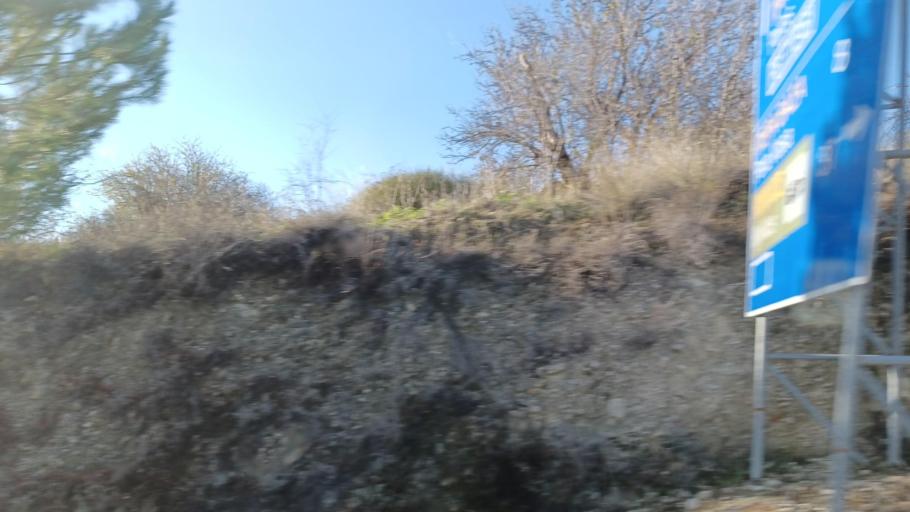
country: CY
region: Limassol
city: Pachna
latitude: 34.8614
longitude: 32.7233
